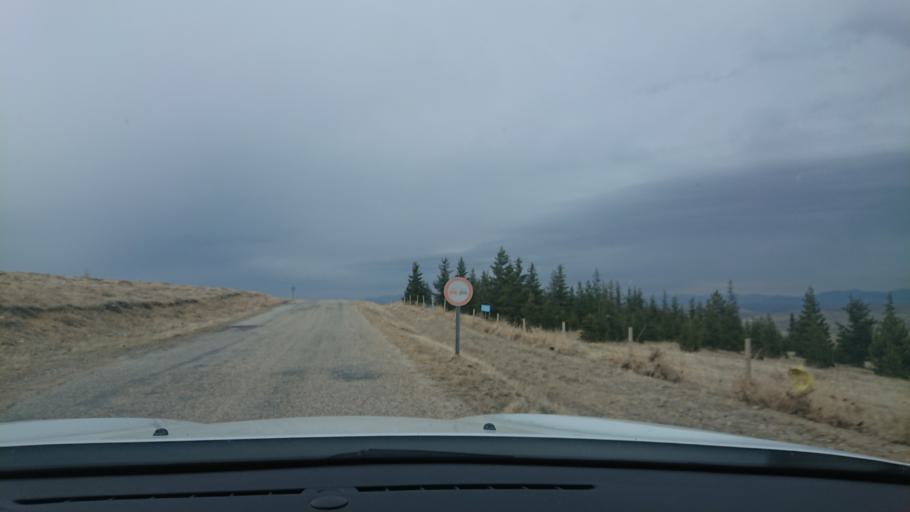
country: TR
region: Aksaray
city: Sariyahsi
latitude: 38.9502
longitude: 33.9019
